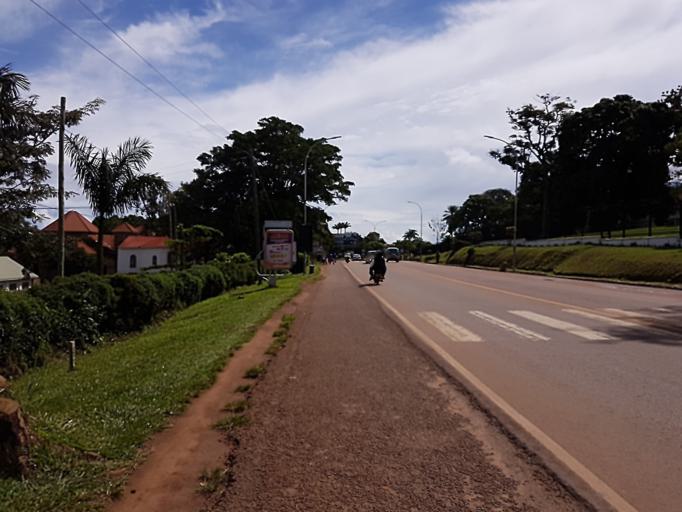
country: UG
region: Central Region
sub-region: Wakiso District
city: Entebbe
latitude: 0.0566
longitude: 32.4706
